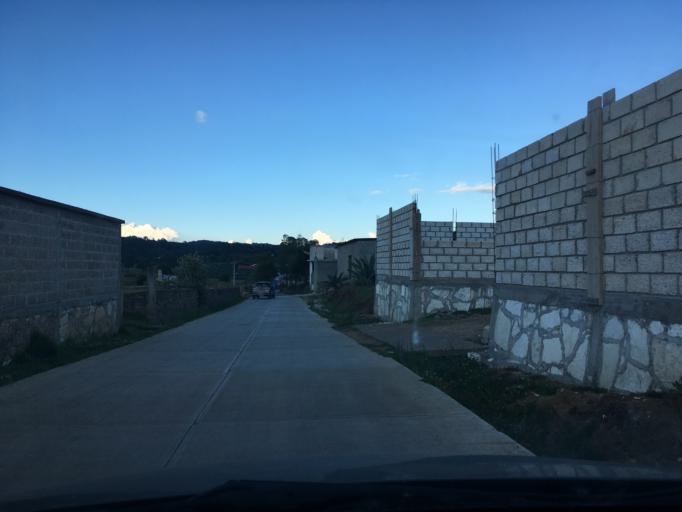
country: MX
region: Hidalgo
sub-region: Omitlan de Juarez
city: San Antonio el Paso
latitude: 20.1456
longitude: -98.6148
